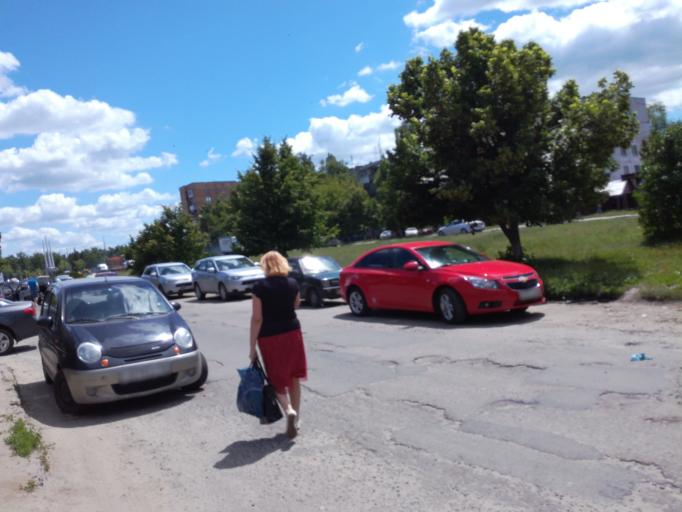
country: RU
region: Kursk
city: Kursk
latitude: 51.7461
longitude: 36.2558
